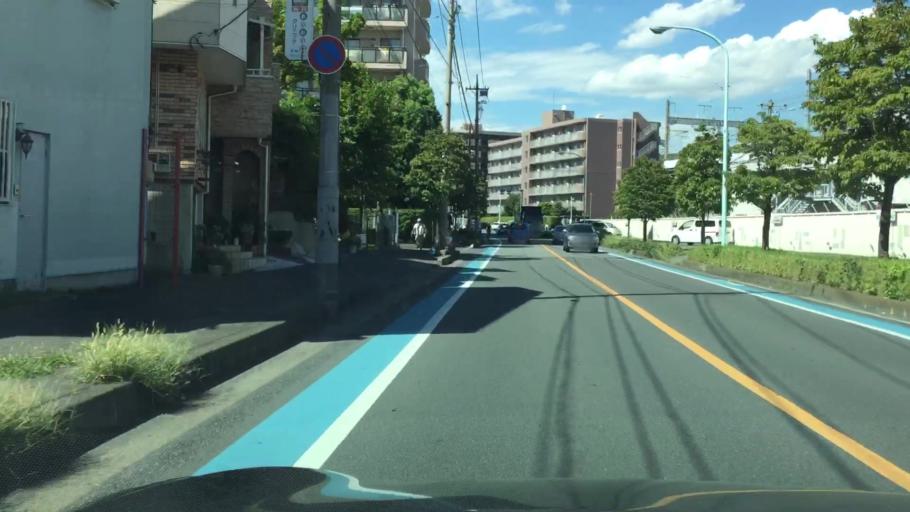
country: JP
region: Saitama
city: Yono
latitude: 35.9145
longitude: 139.6185
